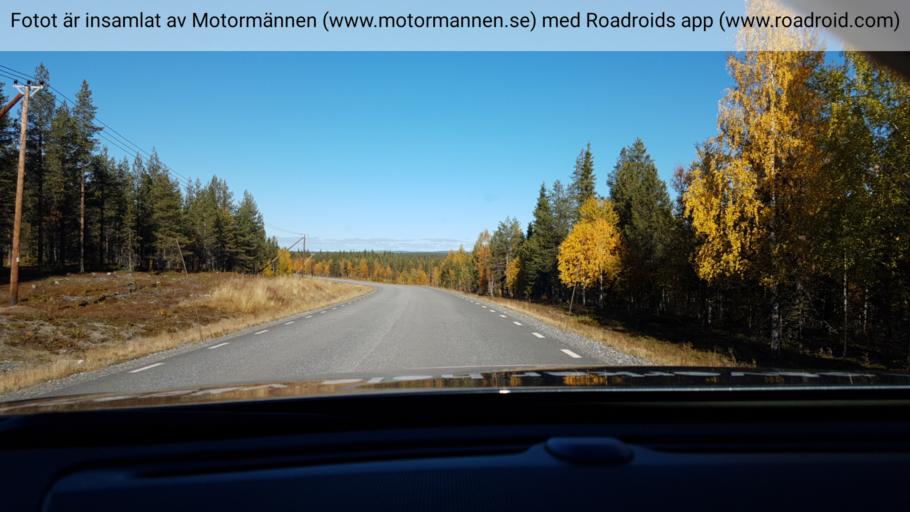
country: SE
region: Norrbotten
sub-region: Gallivare Kommun
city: Gaellivare
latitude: 66.7733
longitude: 21.0527
